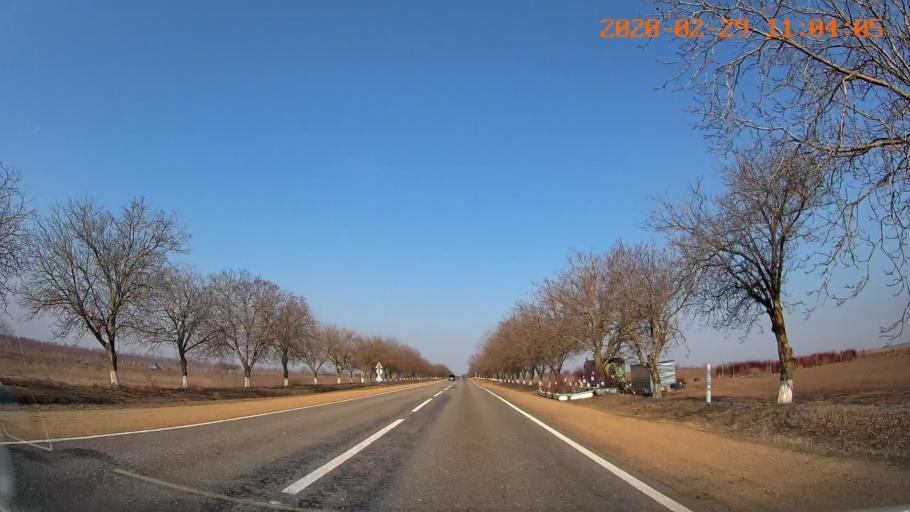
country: MD
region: Criuleni
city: Criuleni
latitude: 47.1845
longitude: 29.2065
